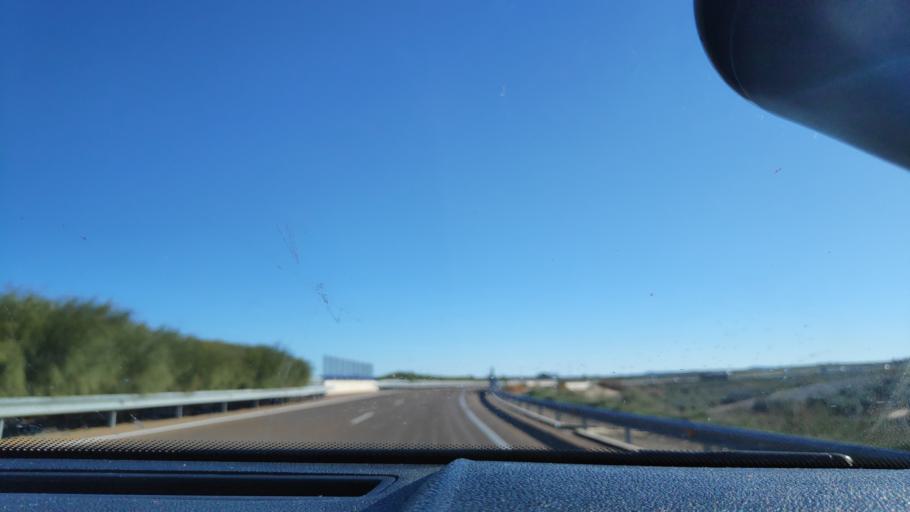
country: ES
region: Extremadura
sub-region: Provincia de Badajoz
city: Villafranca de los Barros
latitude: 38.5297
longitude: -6.3522
